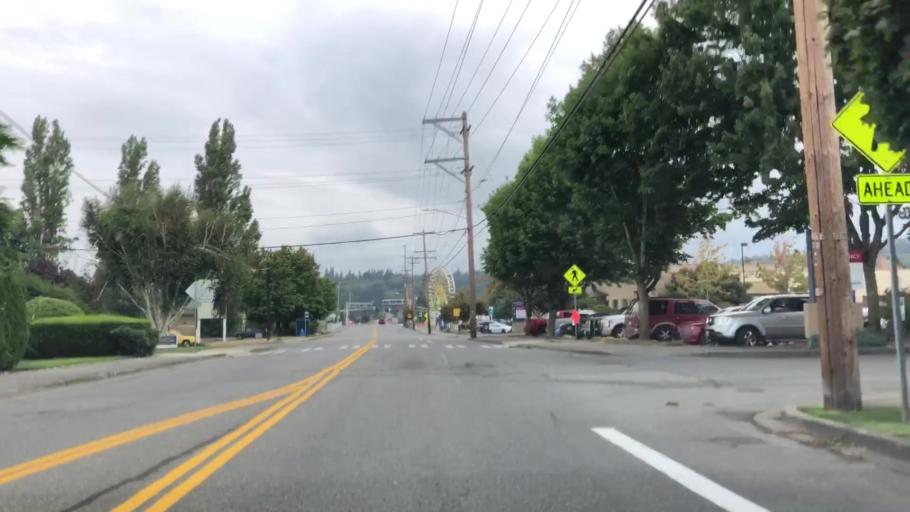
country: US
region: Washington
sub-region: Snohomish County
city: Monroe
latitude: 47.8632
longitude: -121.9906
